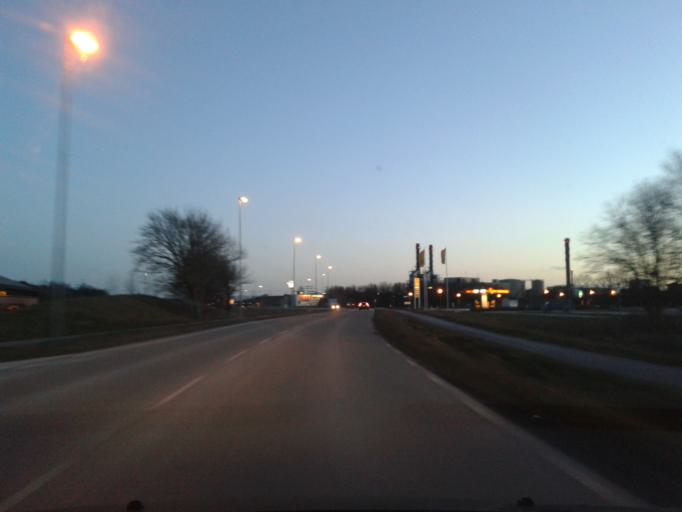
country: SE
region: Gotland
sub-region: Gotland
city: Visby
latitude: 57.6279
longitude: 18.3175
